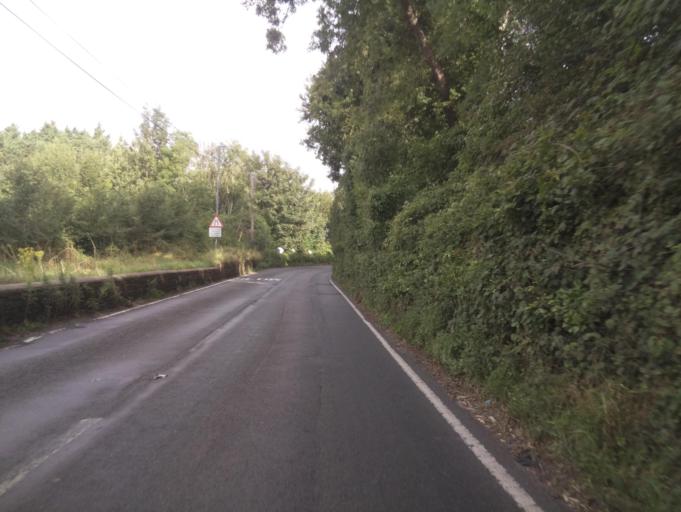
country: GB
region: England
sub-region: North Somerset
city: Nailsea
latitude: 51.4389
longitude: -2.7259
